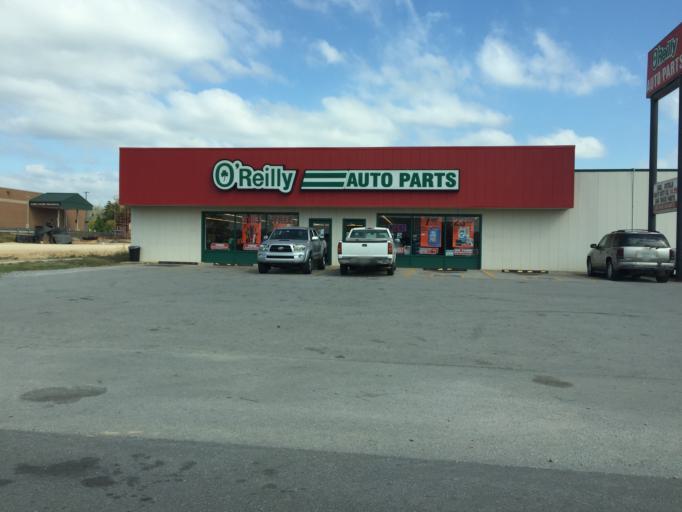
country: US
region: Tennessee
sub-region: Hamilton County
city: Collegedale
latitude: 35.0824
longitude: -85.0573
